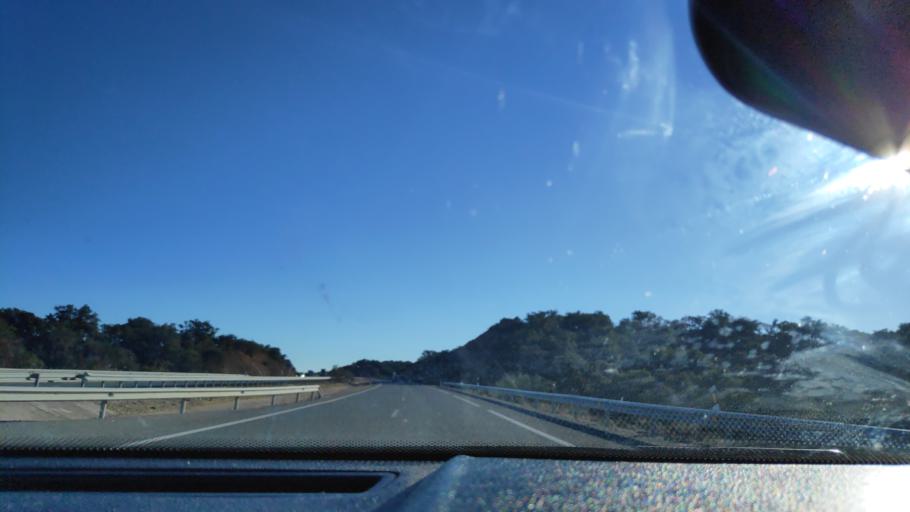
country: ES
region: Andalusia
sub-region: Provincia de Huelva
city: Santa Olalla del Cala
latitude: 37.8782
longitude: -6.2209
